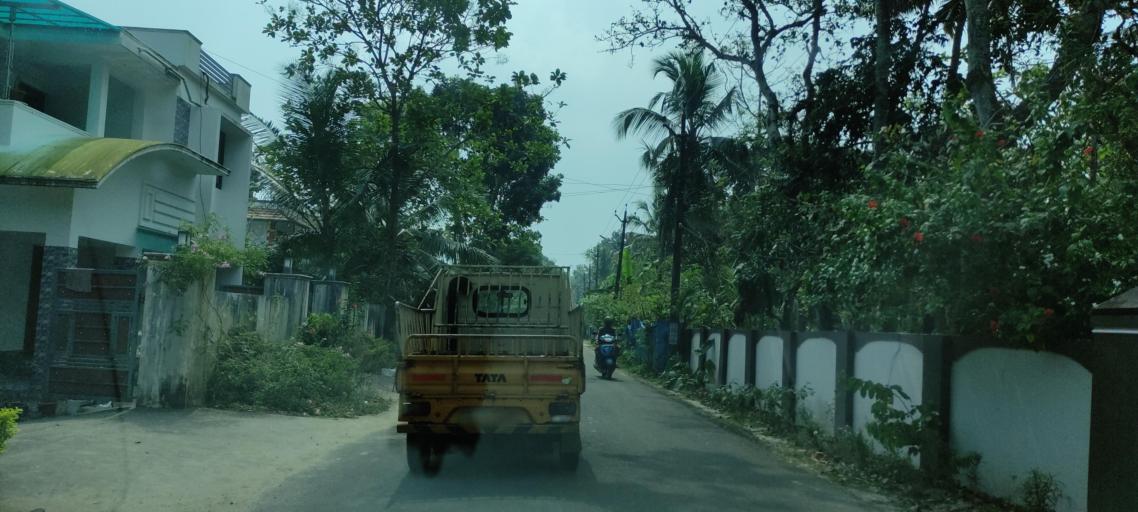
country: IN
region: Kerala
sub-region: Alappuzha
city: Shertallai
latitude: 9.6161
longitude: 76.3476
